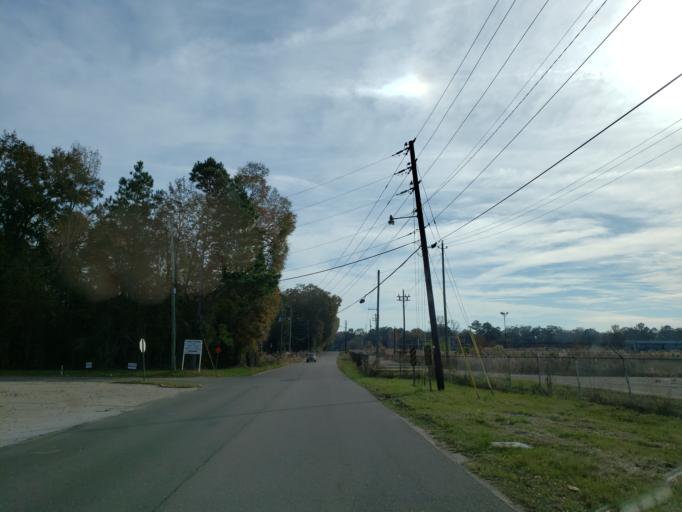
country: US
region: Mississippi
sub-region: Forrest County
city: Hattiesburg
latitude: 31.3397
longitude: -89.3043
